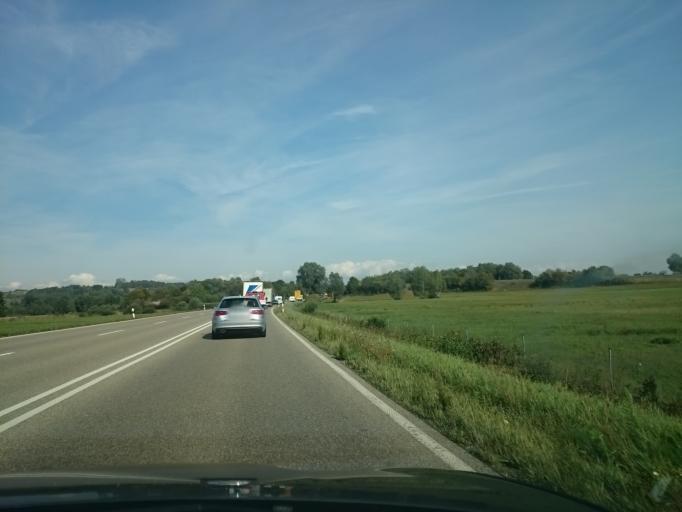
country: DE
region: Bavaria
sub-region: Upper Bavaria
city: Pornbach
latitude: 48.6204
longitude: 11.4414
